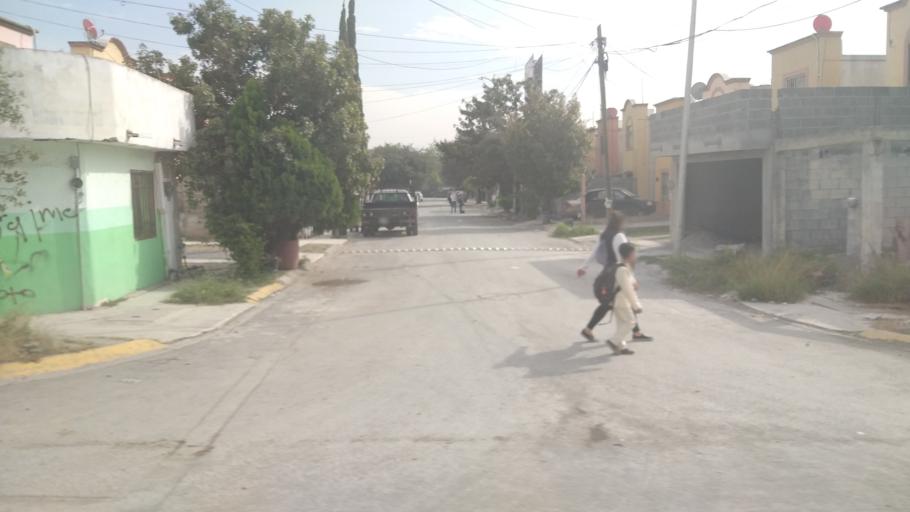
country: MX
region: Nuevo Leon
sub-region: Apodaca
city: Loma la Paz
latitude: 25.7049
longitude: -100.1423
